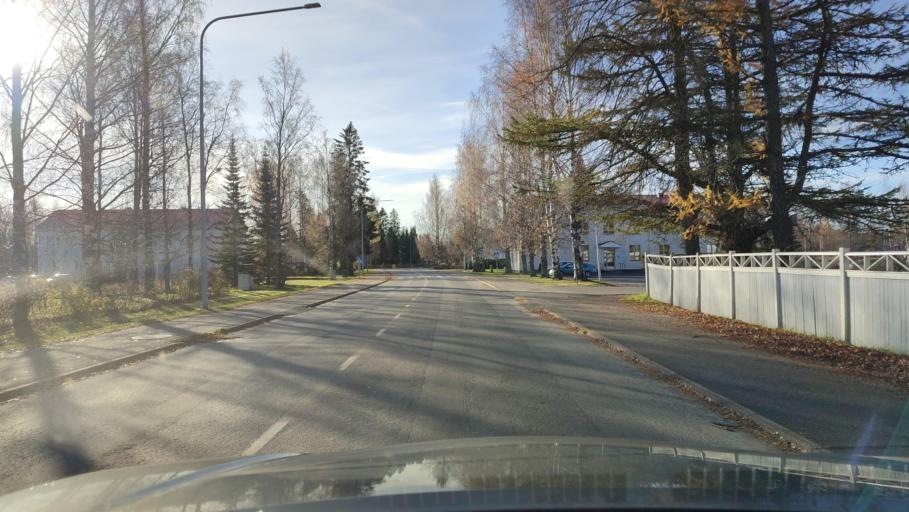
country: FI
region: Southern Ostrobothnia
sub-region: Suupohja
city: Teuva
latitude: 62.4834
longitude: 21.7443
